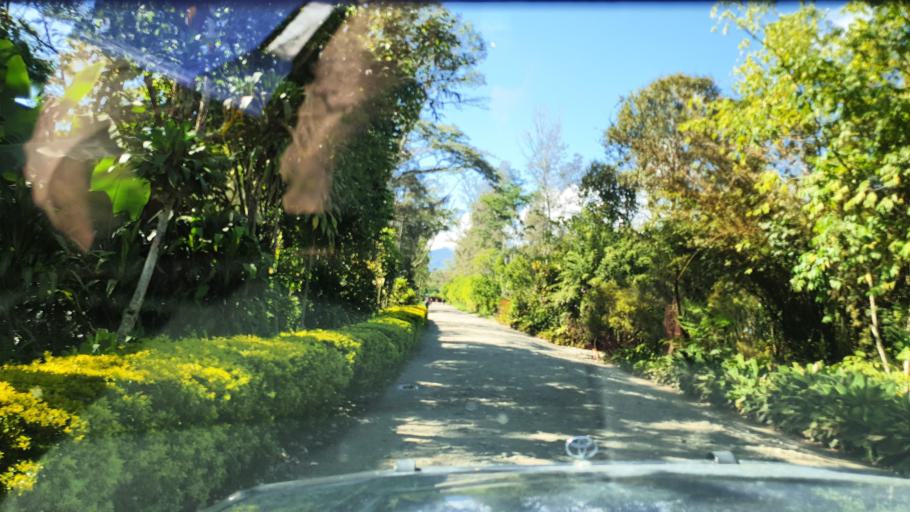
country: PG
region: Western Highlands
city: Rauna
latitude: -5.8215
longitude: 144.3850
